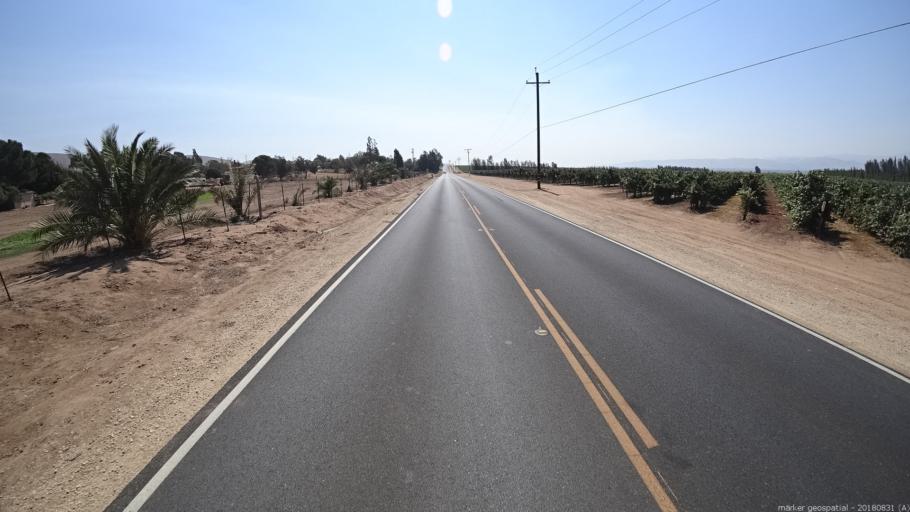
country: US
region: California
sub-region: Monterey County
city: Soledad
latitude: 36.4227
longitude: -121.2864
